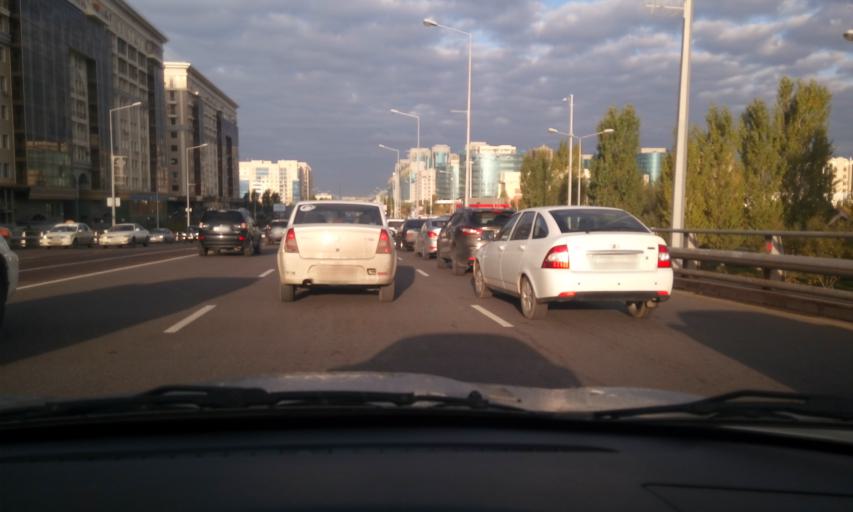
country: KZ
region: Astana Qalasy
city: Astana
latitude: 51.1326
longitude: 71.4385
